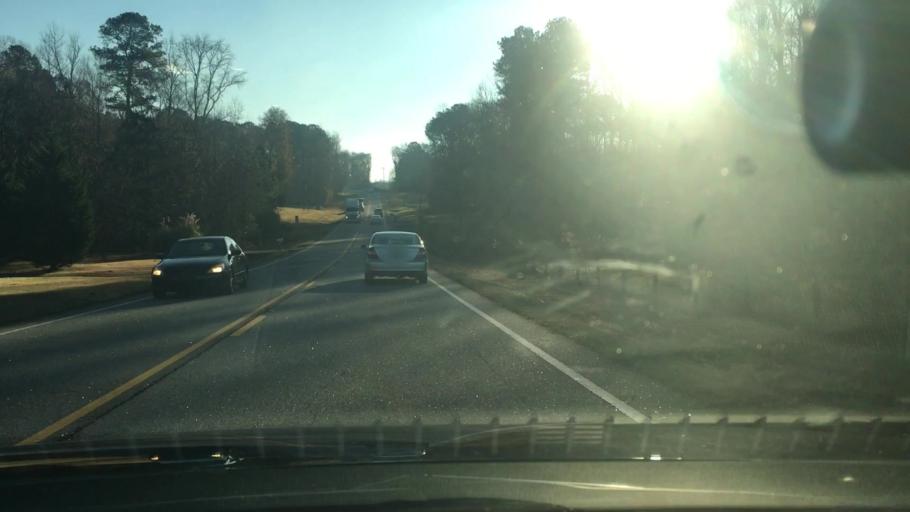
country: US
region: Georgia
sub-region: Spalding County
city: Experiment
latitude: 33.2397
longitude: -84.4092
